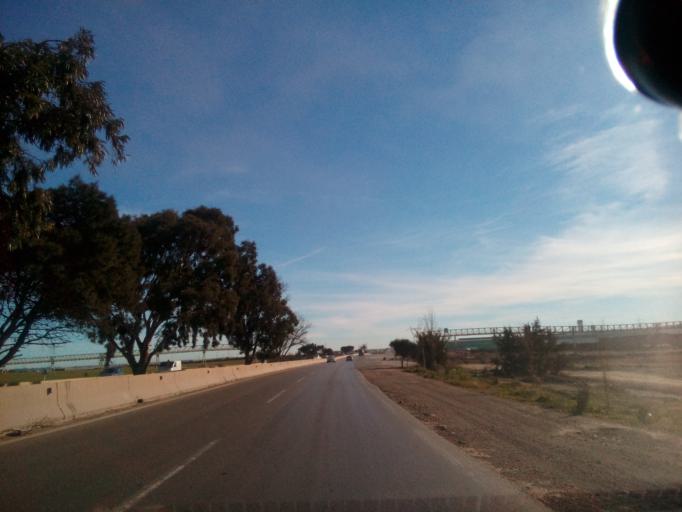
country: DZ
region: Oran
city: Ain el Bya
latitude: 35.7789
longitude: -0.2670
